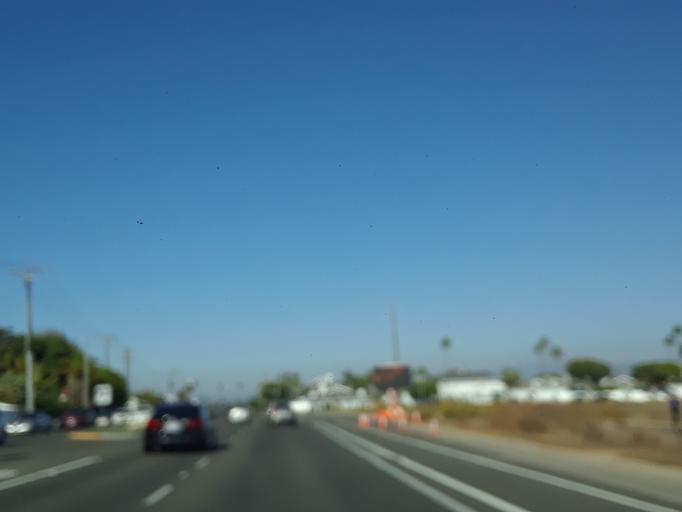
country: US
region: California
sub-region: Orange County
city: Costa Mesa
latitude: 33.6545
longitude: -117.8883
